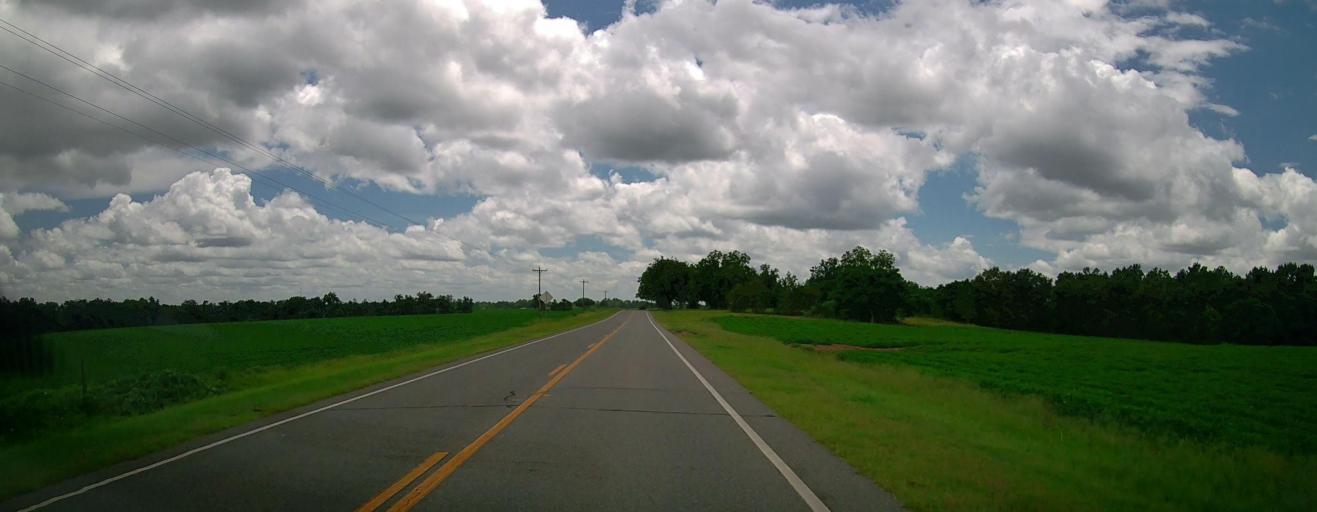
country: US
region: Georgia
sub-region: Wilcox County
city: Rochelle
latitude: 31.9795
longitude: -83.5459
